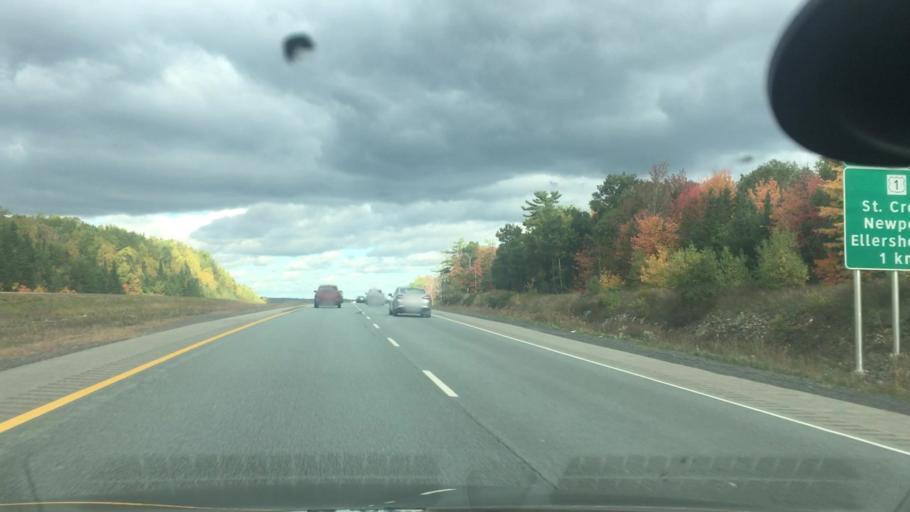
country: CA
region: Nova Scotia
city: Windsor
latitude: 44.9485
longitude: -64.0056
